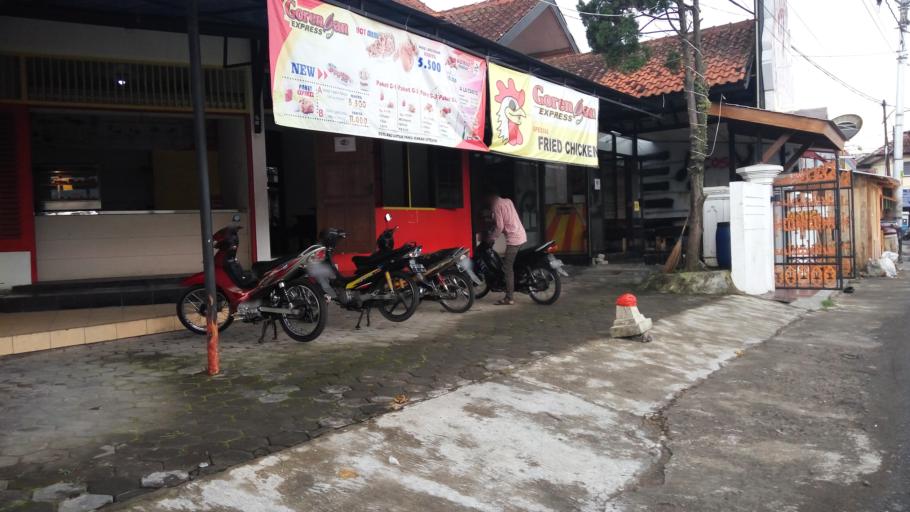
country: ID
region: Central Java
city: Ambarawa
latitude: -7.2644
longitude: 110.4041
